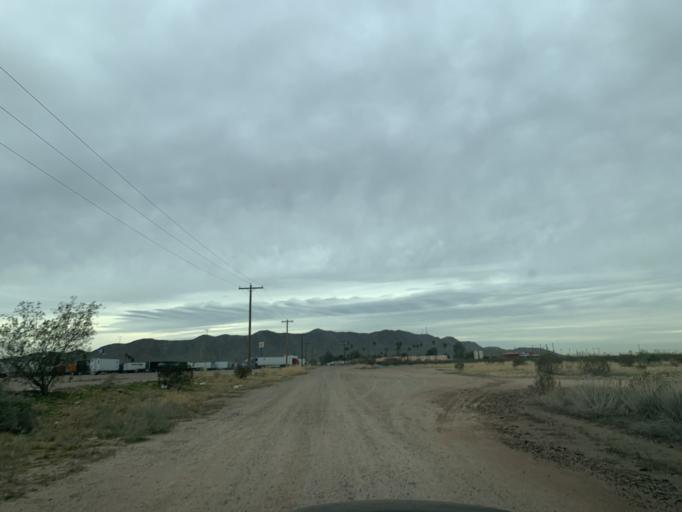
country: US
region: Arizona
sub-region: Pinal County
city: Arizona City
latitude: 32.8140
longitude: -111.6669
